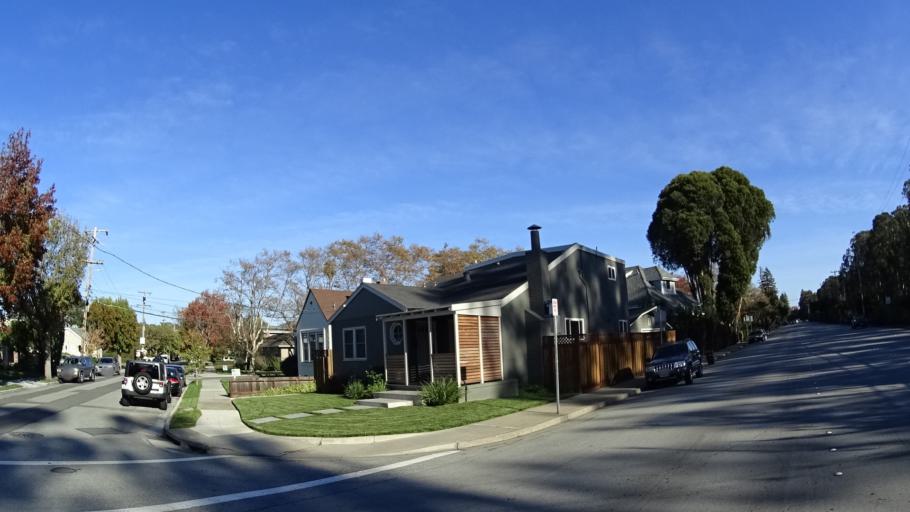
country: US
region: California
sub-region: San Mateo County
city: Burlingame
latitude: 37.5848
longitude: -122.3551
